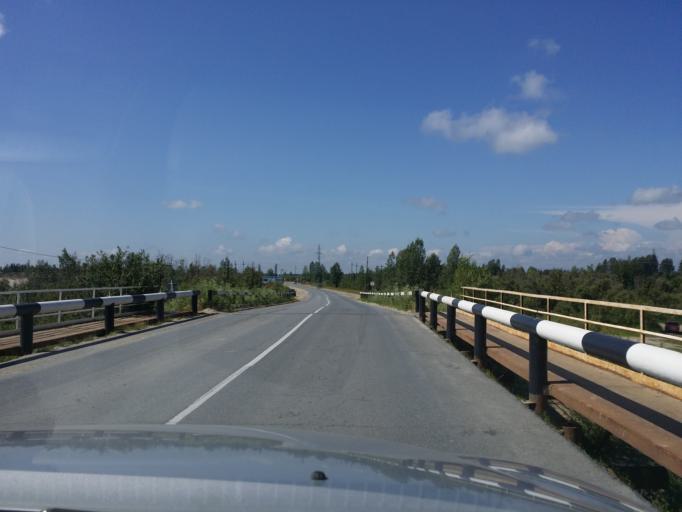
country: RU
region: Khanty-Mansiyskiy Avtonomnyy Okrug
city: Nizhnevartovsk
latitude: 61.0324
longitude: 76.3506
